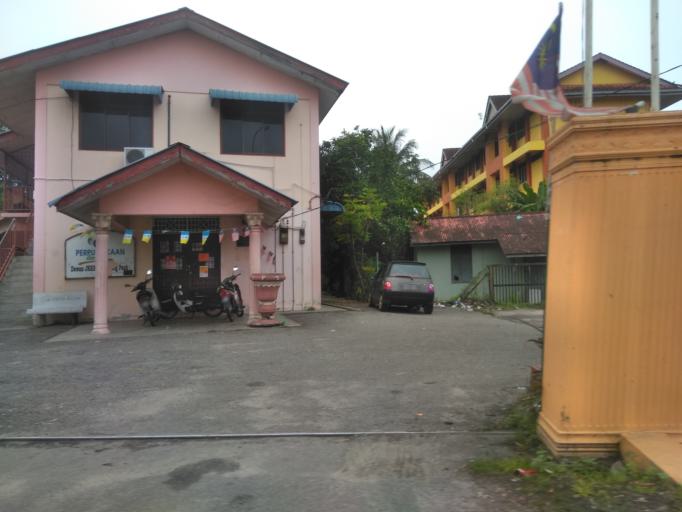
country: MY
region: Penang
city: Perai
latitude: 5.4108
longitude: 100.4135
